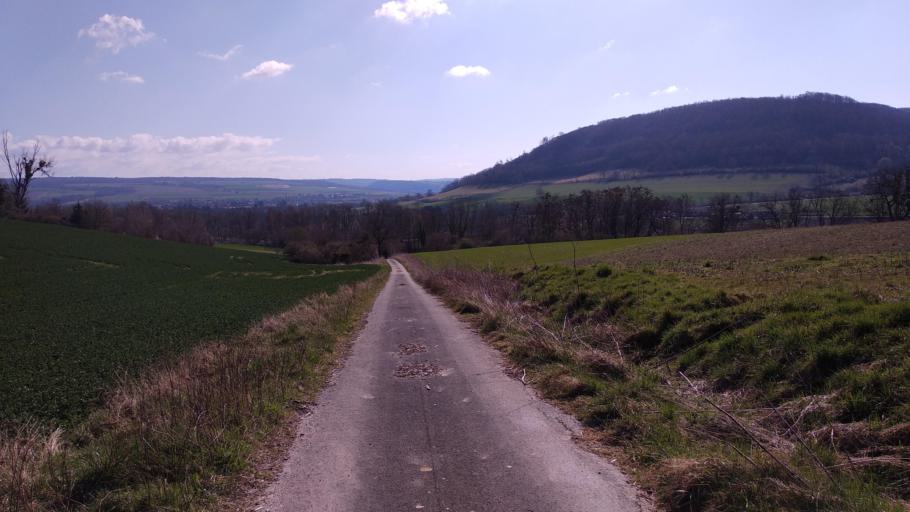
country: DE
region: North Rhine-Westphalia
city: Beverungen
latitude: 51.6593
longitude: 9.3441
